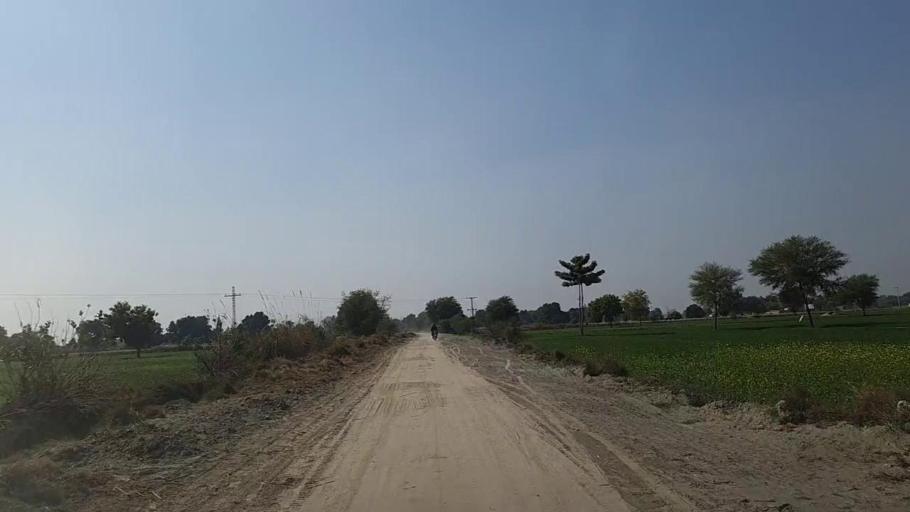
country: PK
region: Sindh
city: Nawabshah
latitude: 26.2449
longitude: 68.4673
